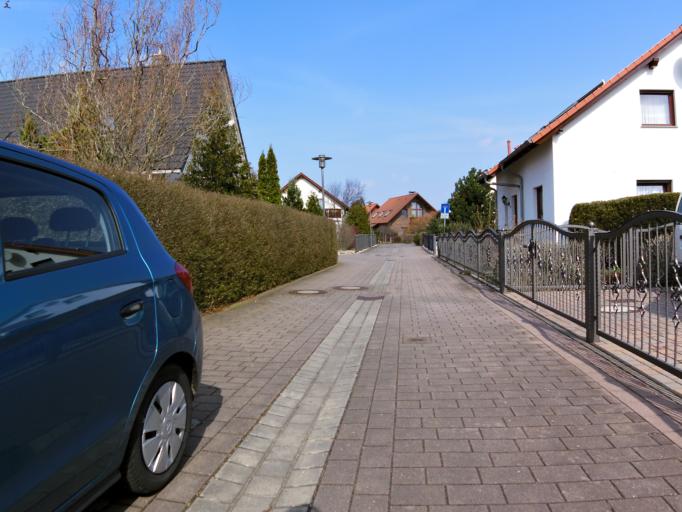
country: DE
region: Saxony
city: Markranstadt
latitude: 51.3073
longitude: 12.2958
